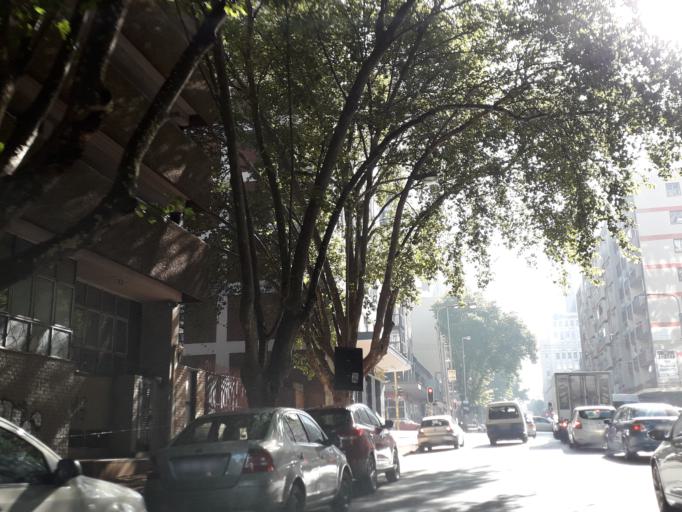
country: ZA
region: Gauteng
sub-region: City of Johannesburg Metropolitan Municipality
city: Johannesburg
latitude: -26.1951
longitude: 28.0366
